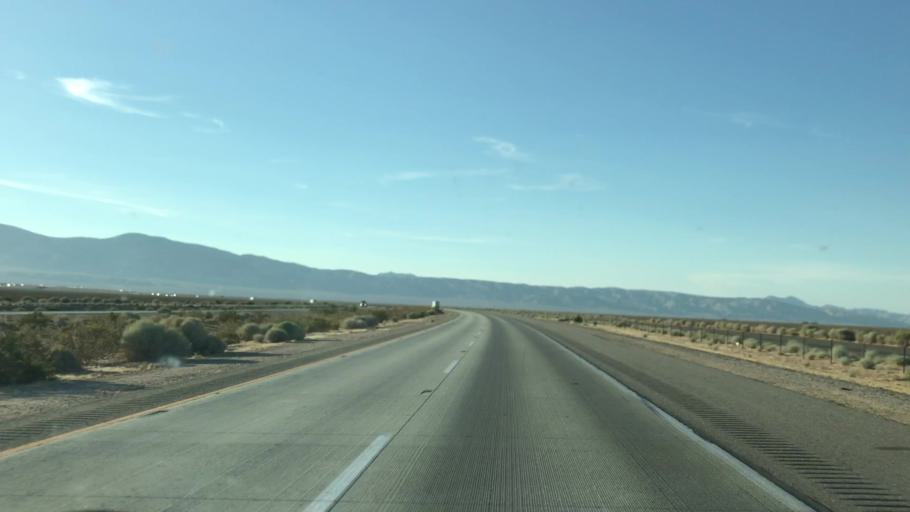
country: US
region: California
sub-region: Kern County
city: Mojave
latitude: 35.0742
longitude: -118.1135
